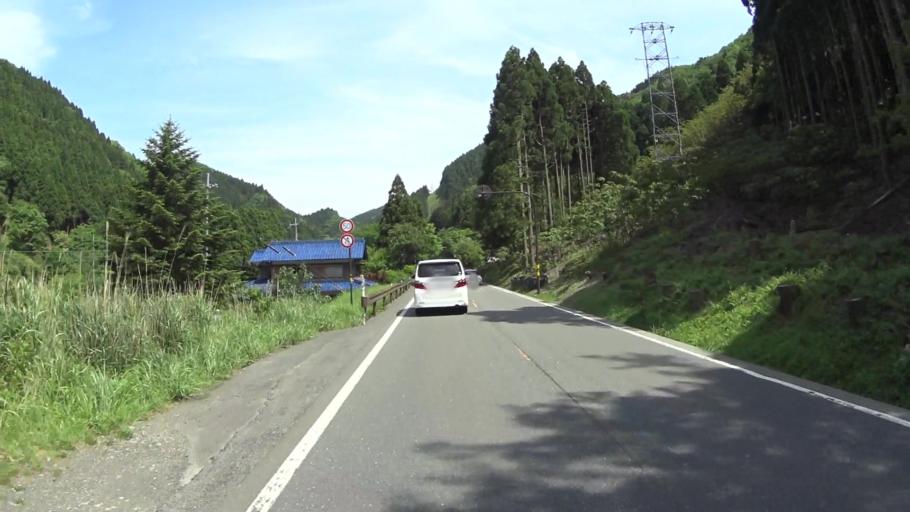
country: JP
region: Fukui
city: Obama
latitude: 35.4388
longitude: 135.9091
